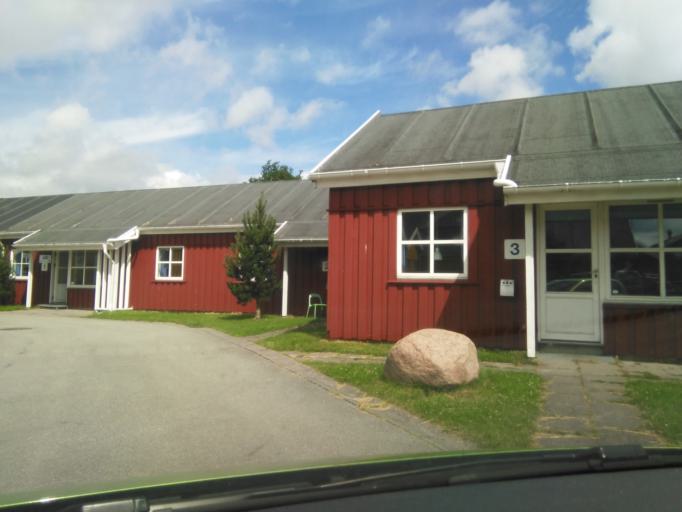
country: DK
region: Central Jutland
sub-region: Arhus Kommune
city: Logten
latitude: 56.2443
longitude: 10.3431
